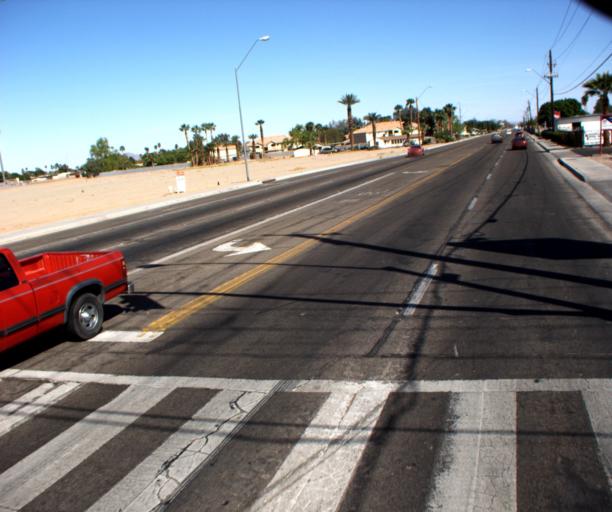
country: US
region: Arizona
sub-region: Yuma County
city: Yuma
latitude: 32.6913
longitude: -114.6504
